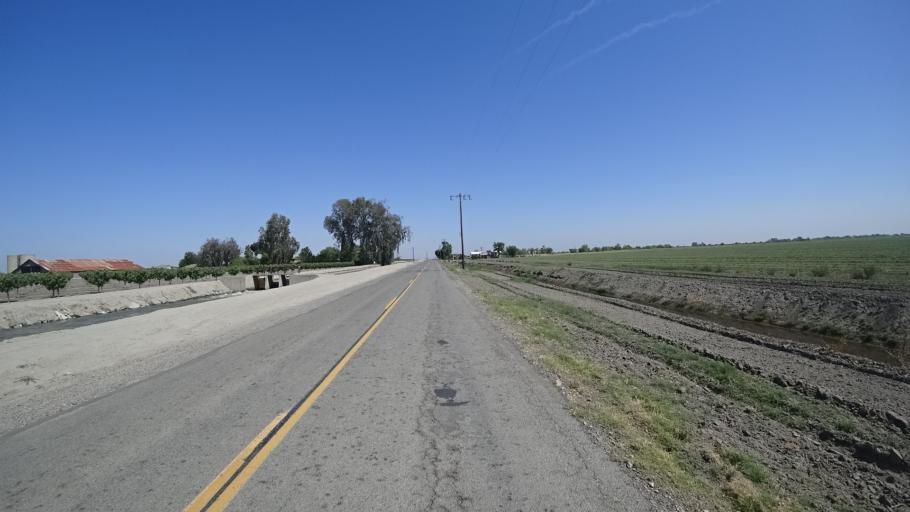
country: US
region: California
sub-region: Kings County
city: Corcoran
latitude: 36.0321
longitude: -119.5361
